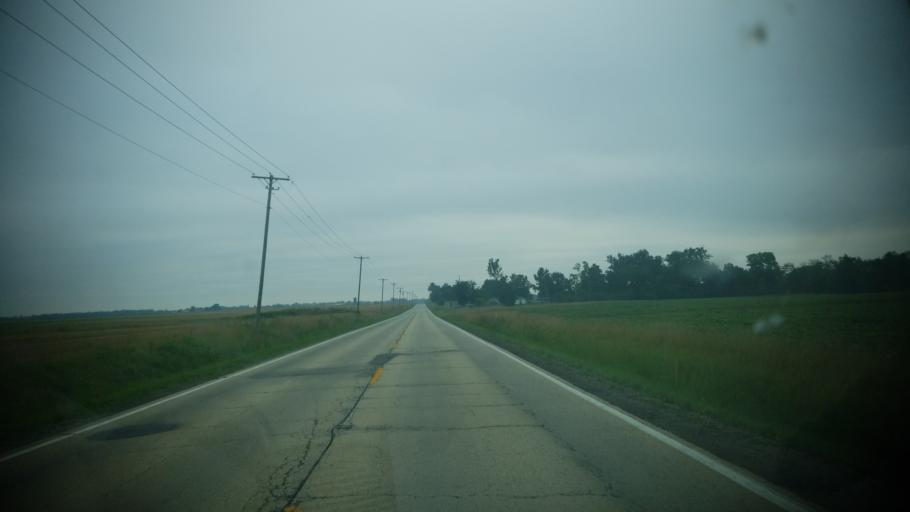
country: US
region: Illinois
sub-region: Clay County
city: Flora
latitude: 38.6526
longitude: -88.4384
